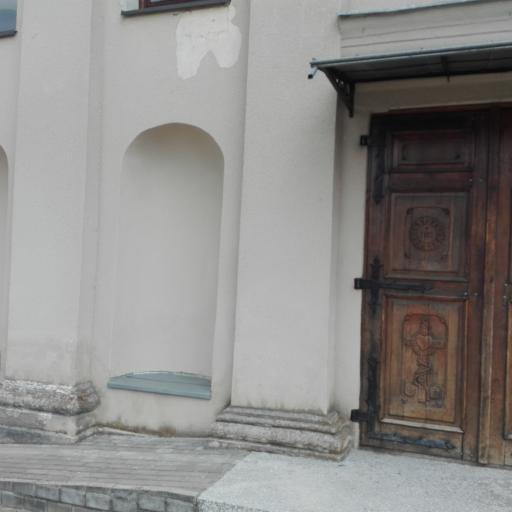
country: LT
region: Vilnius County
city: Ukmerge
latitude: 55.2139
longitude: 24.7882
